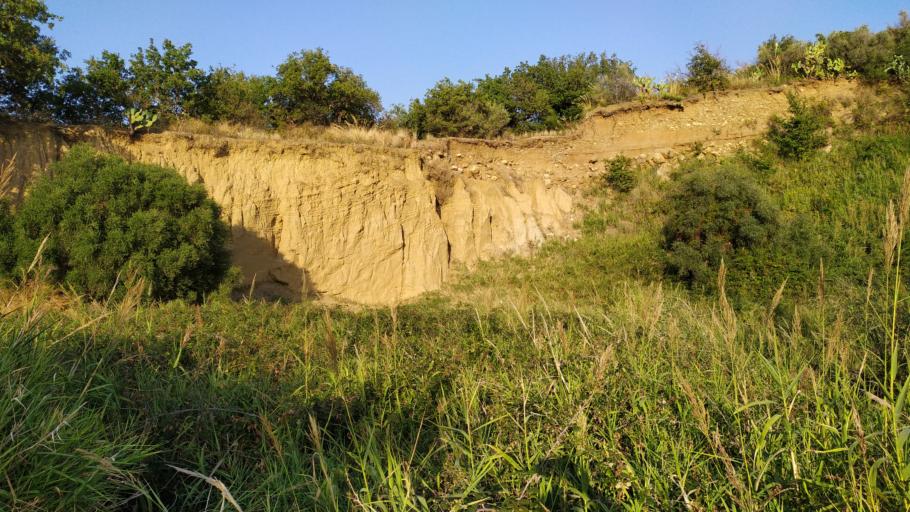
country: IT
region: Sicily
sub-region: Messina
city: Saponara Marittima
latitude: 38.2256
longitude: 15.4284
